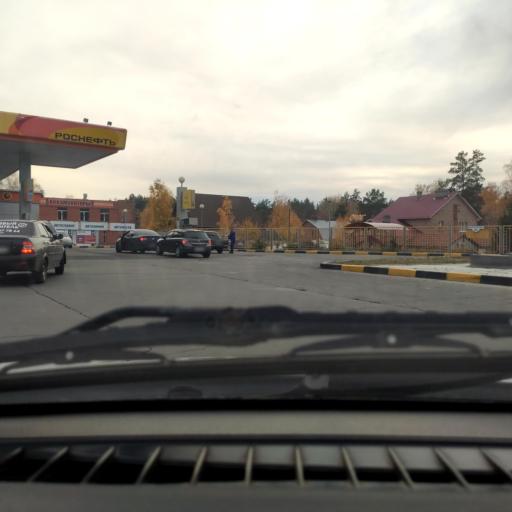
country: RU
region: Samara
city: Zhigulevsk
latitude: 53.4978
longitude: 49.4720
